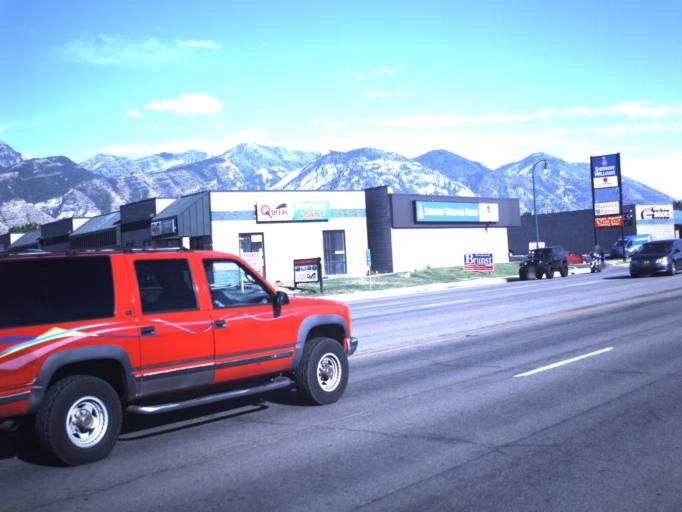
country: US
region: Utah
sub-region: Utah County
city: Orem
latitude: 40.3024
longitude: -111.6975
